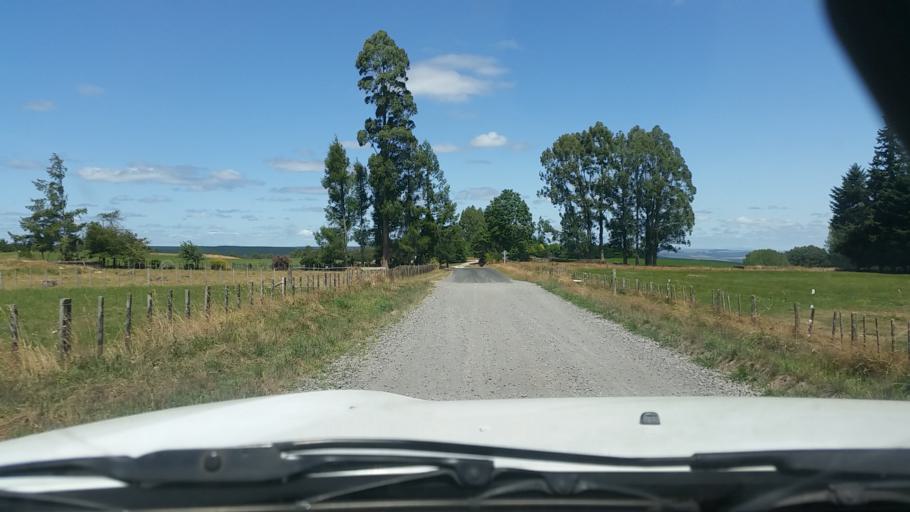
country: NZ
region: Bay of Plenty
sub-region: Whakatane District
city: Murupara
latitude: -38.4786
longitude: 176.4147
